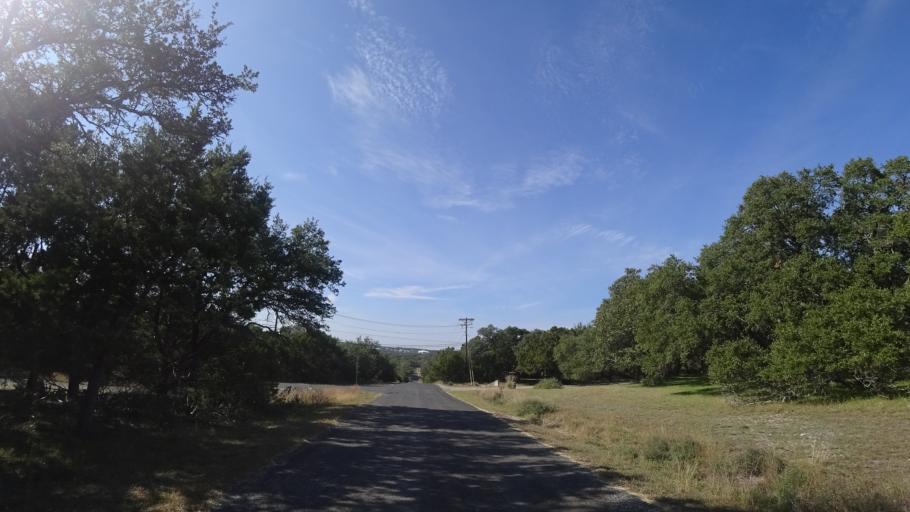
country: US
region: Texas
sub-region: Travis County
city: Barton Creek
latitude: 30.2241
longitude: -97.9097
